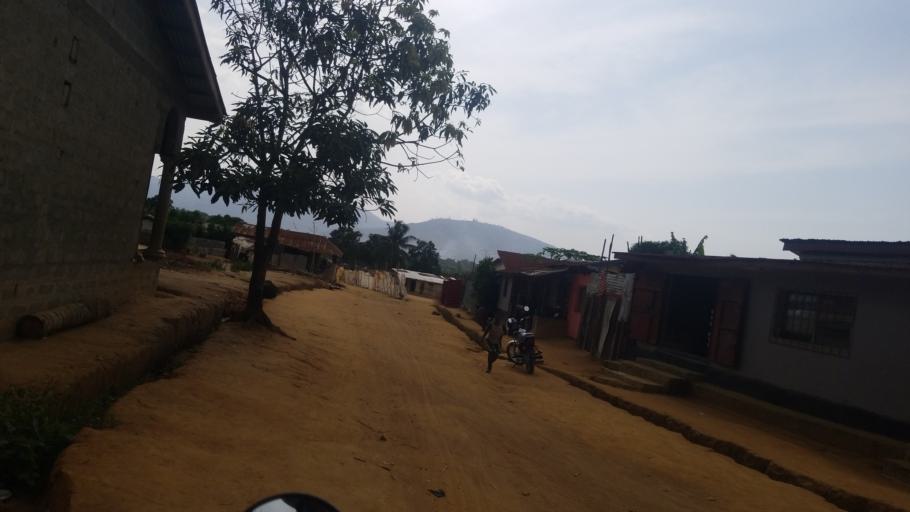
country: SL
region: Western Area
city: Waterloo
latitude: 8.3207
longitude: -13.0484
